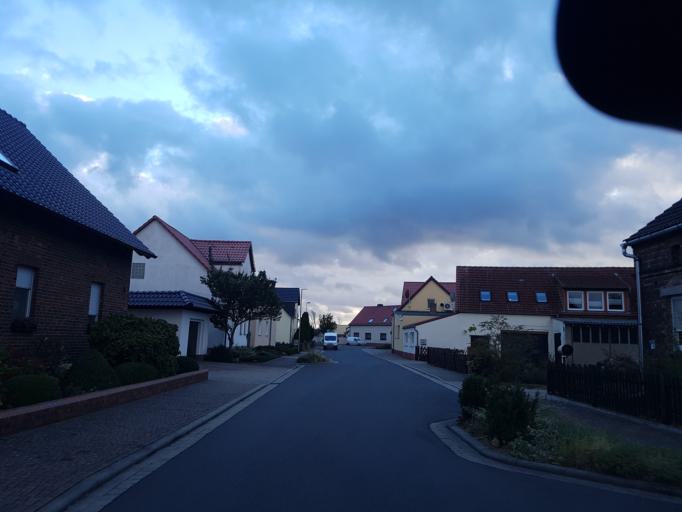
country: DE
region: Saxony-Anhalt
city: Elster
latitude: 51.8213
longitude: 12.8540
